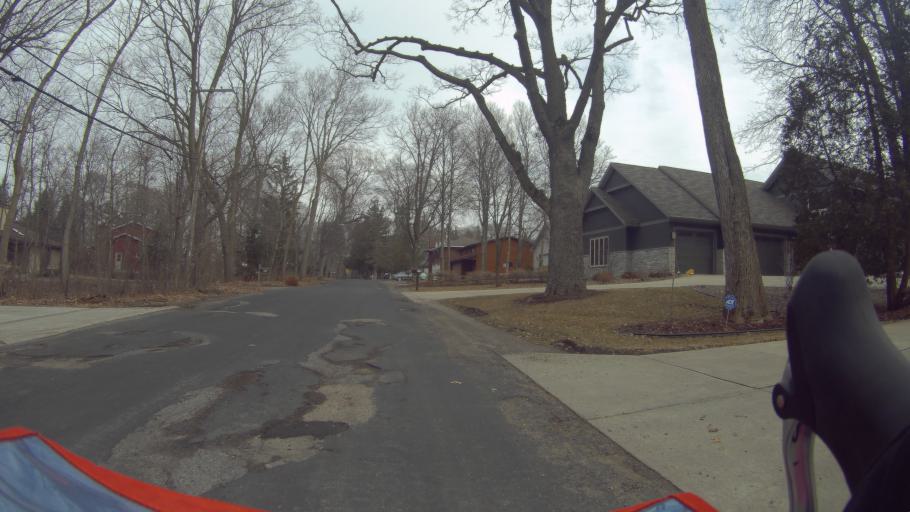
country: US
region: Wisconsin
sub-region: Dane County
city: Maple Bluff
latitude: 43.1304
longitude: -89.3842
